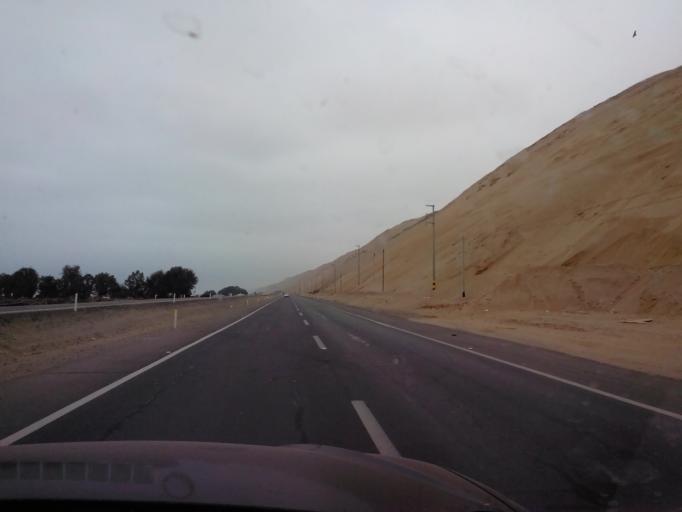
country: PE
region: Ica
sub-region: Provincia de Chincha
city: San Pedro
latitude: -13.3641
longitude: -76.2147
